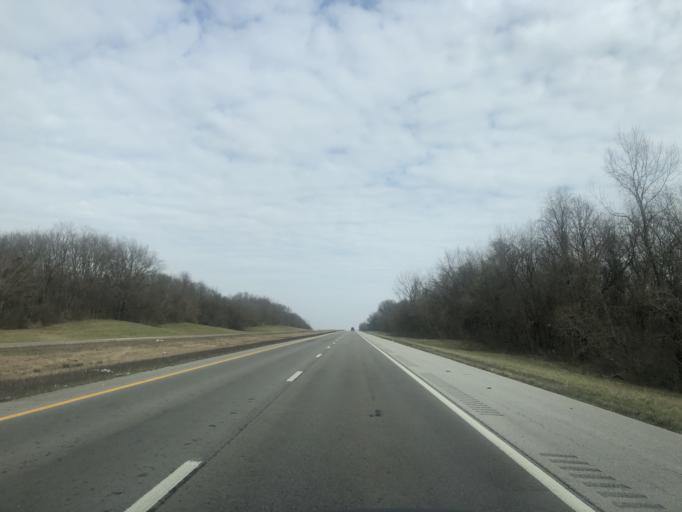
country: US
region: Tennessee
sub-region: Maury County
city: Mount Pleasant
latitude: 35.5758
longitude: -87.1523
